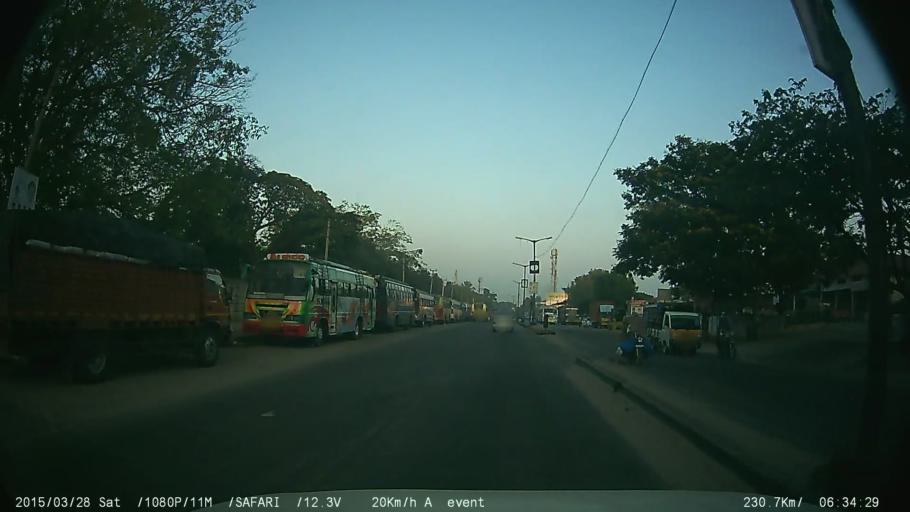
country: IN
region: Karnataka
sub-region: Ramanagara
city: Channapatna
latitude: 12.6522
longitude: 77.2050
